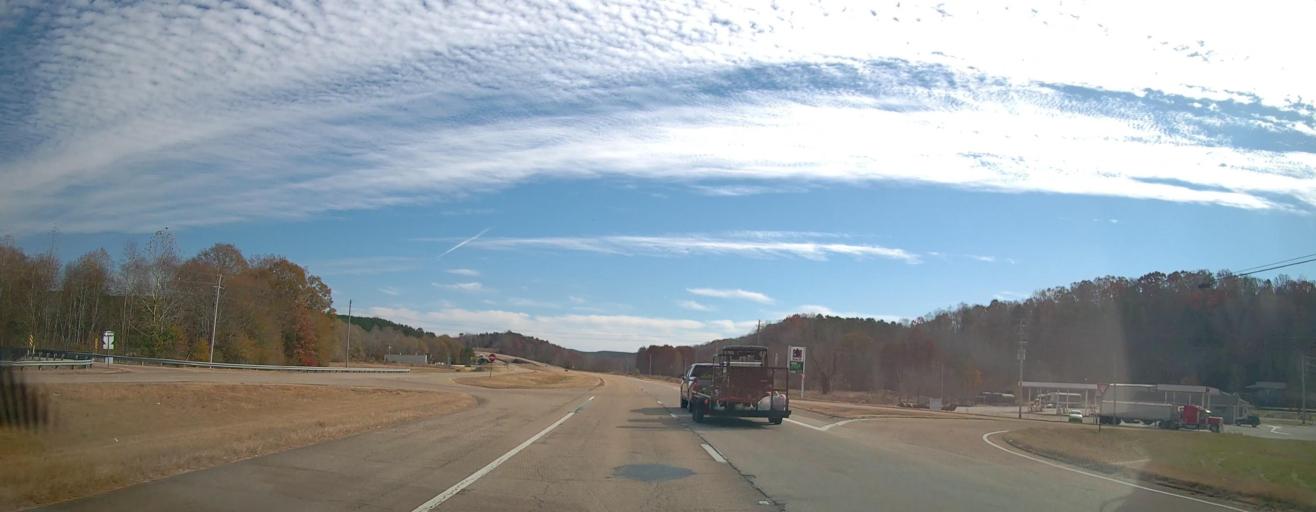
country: US
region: Mississippi
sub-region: Alcorn County
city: Corinth
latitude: 34.9364
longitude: -88.7748
